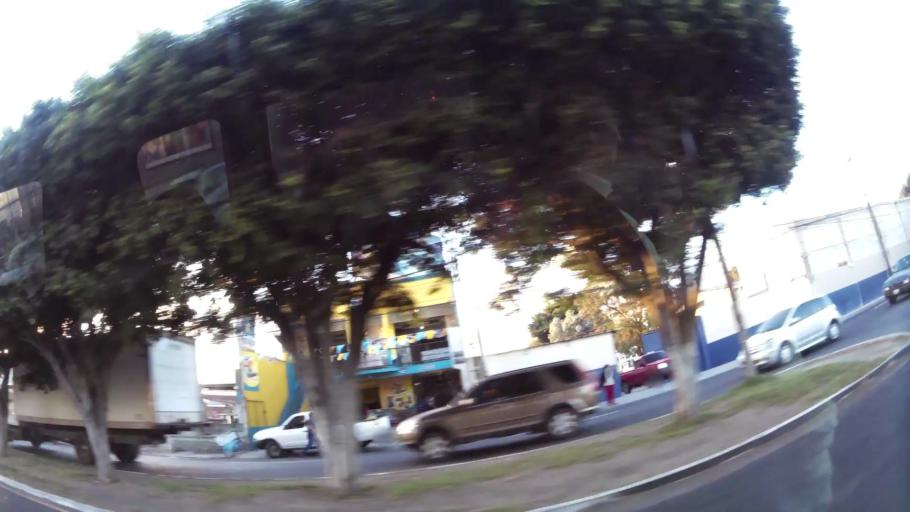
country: GT
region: Guatemala
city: Villa Nueva
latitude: 14.5143
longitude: -90.5778
